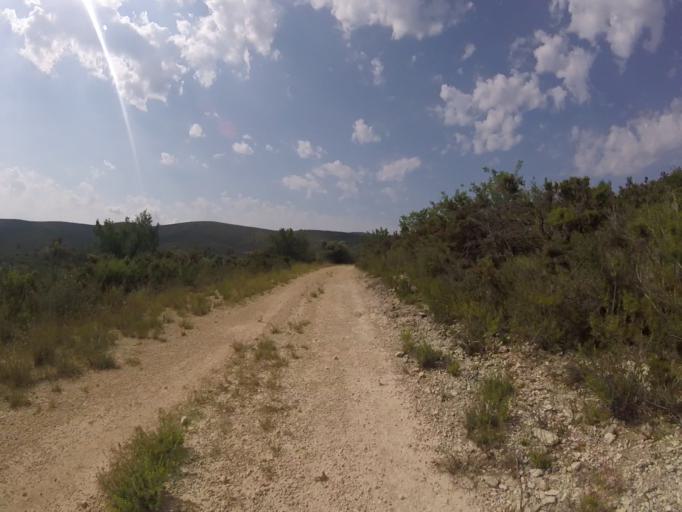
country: ES
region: Valencia
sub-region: Provincia de Castello
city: Alcala de Xivert
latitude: 40.3380
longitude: 0.1964
